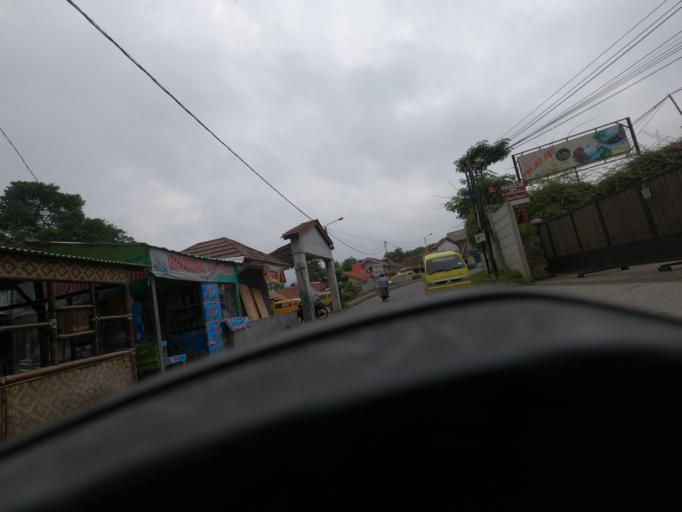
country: ID
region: West Java
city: Lembang
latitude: -6.7987
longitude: 107.5760
